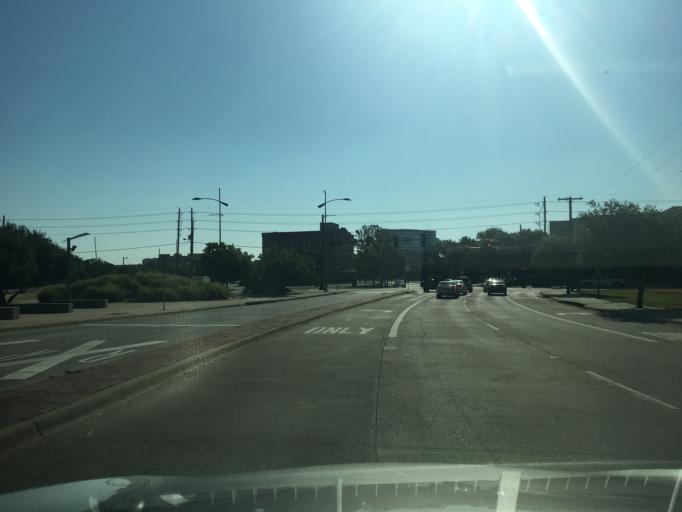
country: US
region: Texas
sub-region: Dallas County
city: Addison
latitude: 32.9576
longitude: -96.8308
